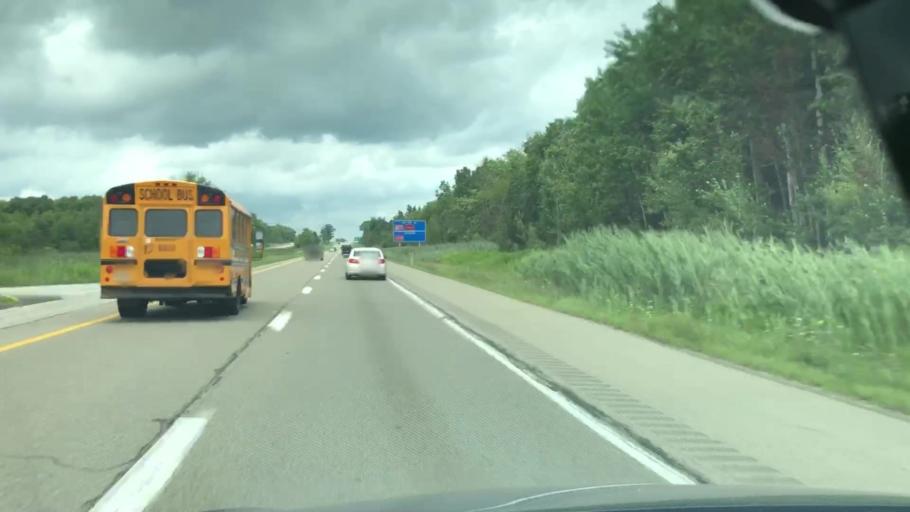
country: US
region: Pennsylvania
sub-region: Erie County
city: Edinboro
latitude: 41.8663
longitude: -80.1763
